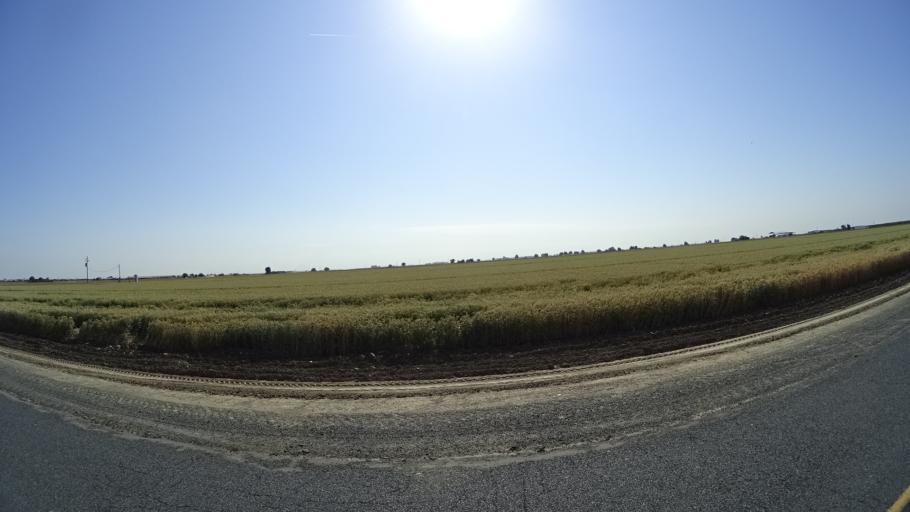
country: US
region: California
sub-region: Kings County
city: Home Garden
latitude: 36.2320
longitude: -119.5831
